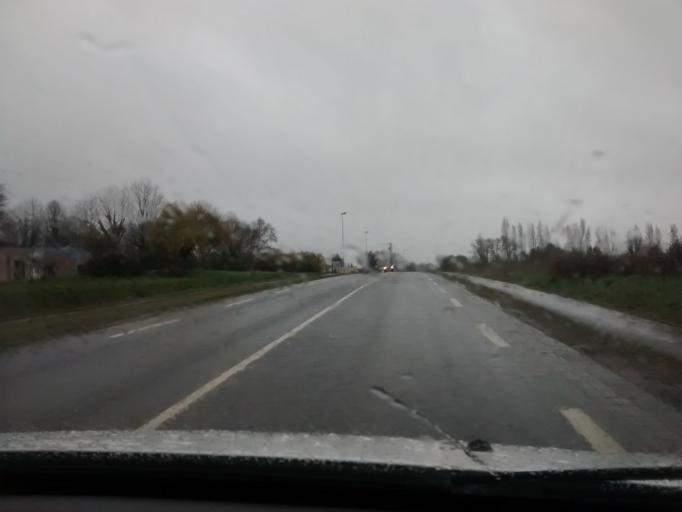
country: FR
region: Brittany
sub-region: Departement d'Ille-et-Vilaine
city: Acigne
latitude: 48.1393
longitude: -1.5603
